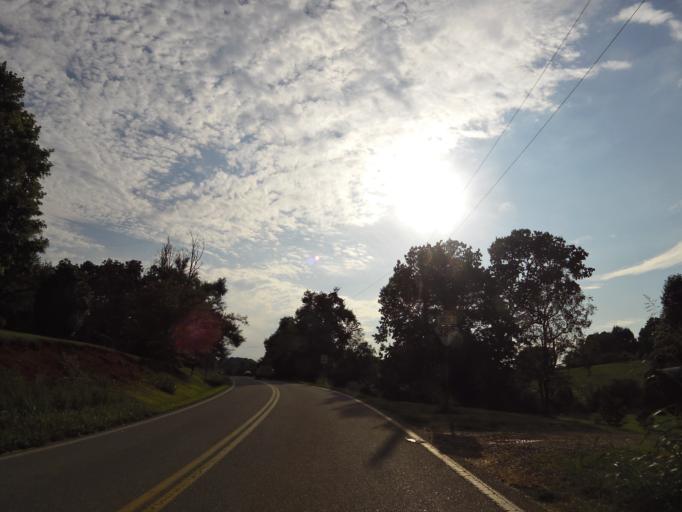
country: US
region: Tennessee
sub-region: Monroe County
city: Vonore
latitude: 35.6285
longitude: -84.3145
